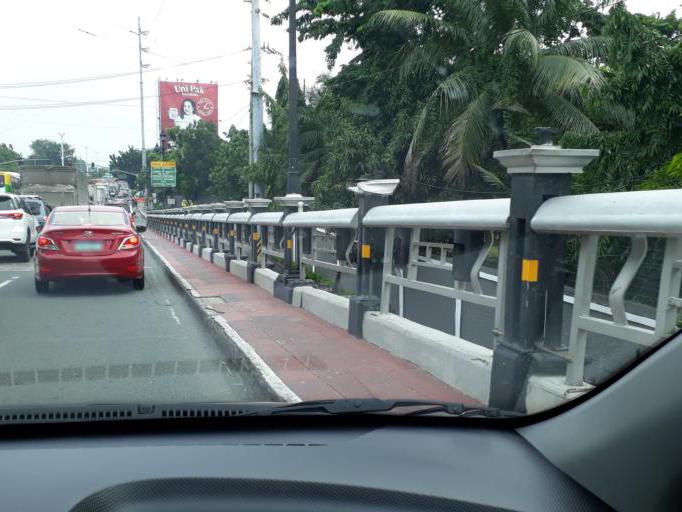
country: PH
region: Metro Manila
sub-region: City of Manila
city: Quiapo
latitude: 14.5944
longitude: 121.0016
